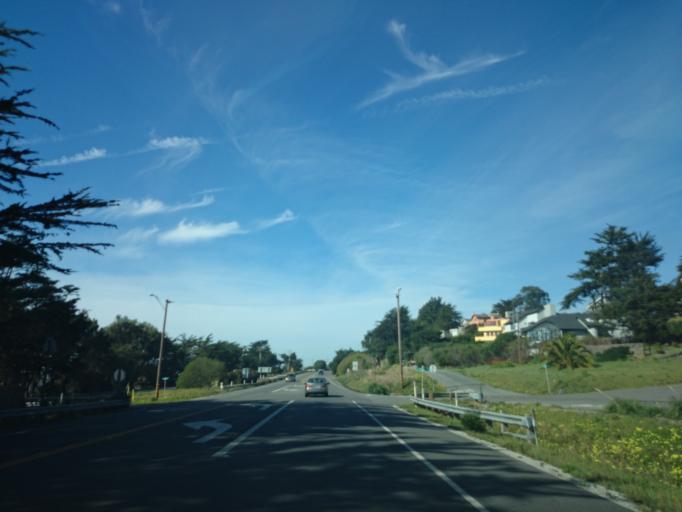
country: US
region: California
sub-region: San Mateo County
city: Moss Beach
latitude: 37.5284
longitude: -122.5142
